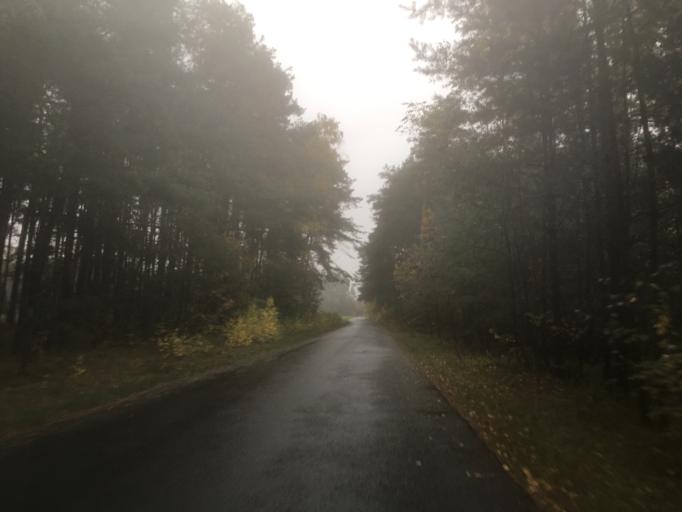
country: DE
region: Brandenburg
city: Neu Zauche
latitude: 52.0291
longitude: 14.0312
